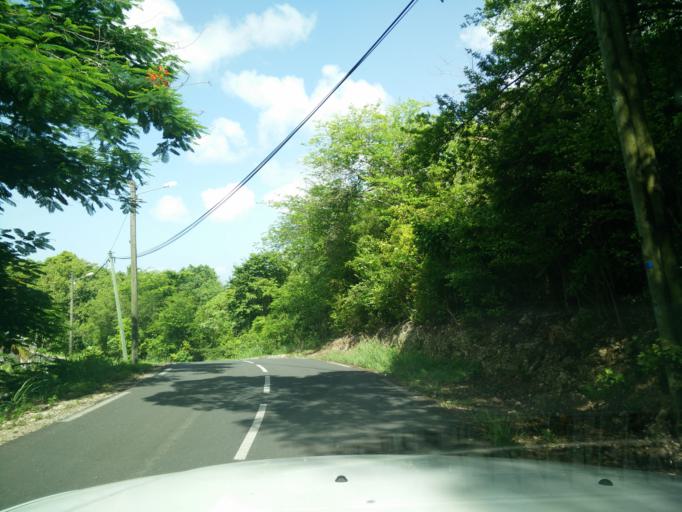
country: GP
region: Guadeloupe
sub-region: Guadeloupe
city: Le Gosier
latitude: 16.2303
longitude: -61.4594
